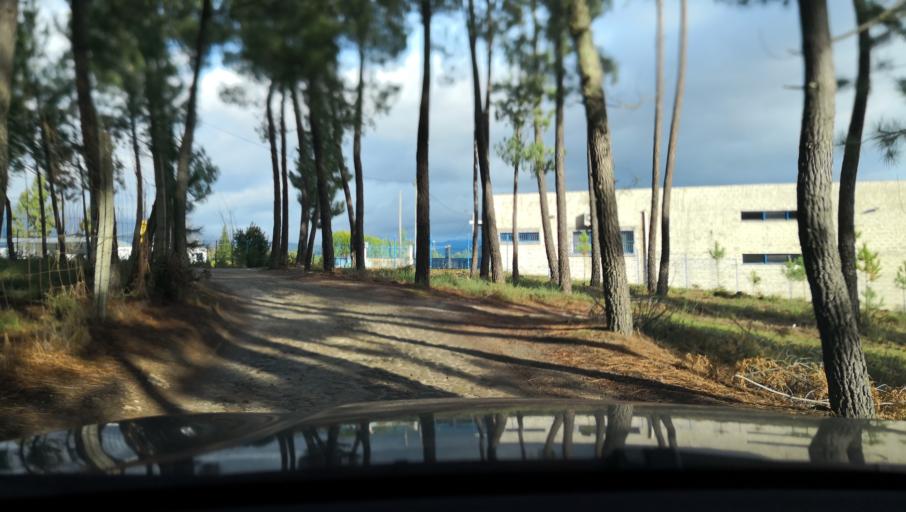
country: PT
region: Vila Real
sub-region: Vila Real
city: Vila Real
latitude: 41.2743
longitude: -7.7158
